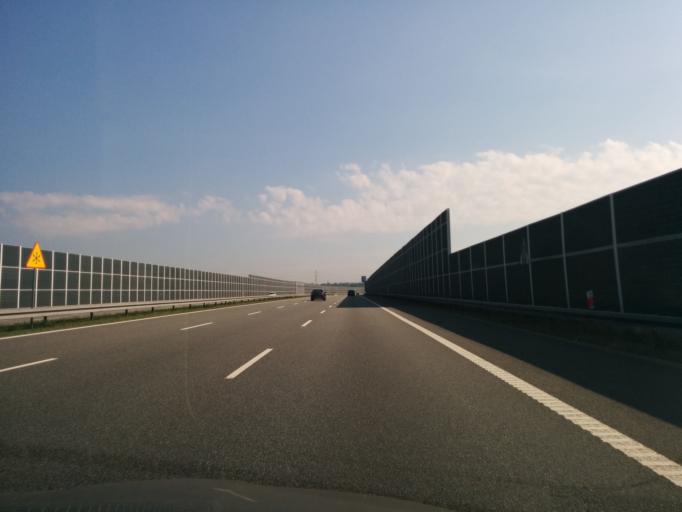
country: PL
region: Silesian Voivodeship
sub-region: Powiat tarnogorski
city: Wieszowa
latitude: 50.3618
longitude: 18.7294
